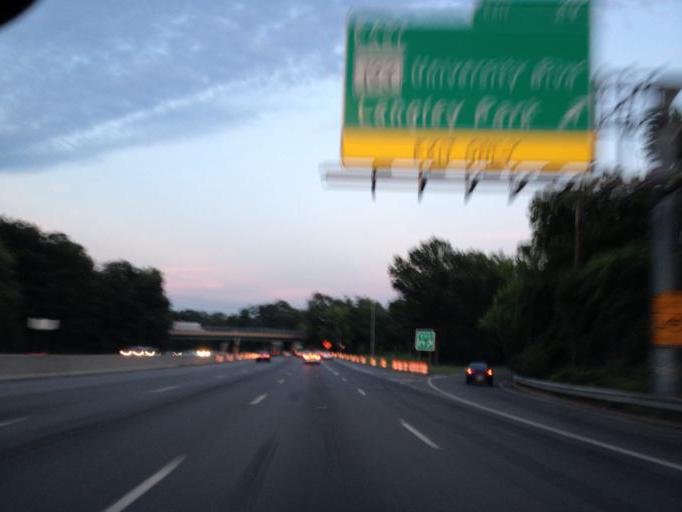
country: US
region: Maryland
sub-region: Montgomery County
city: Four Corners
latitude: 39.0158
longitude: -77.0079
